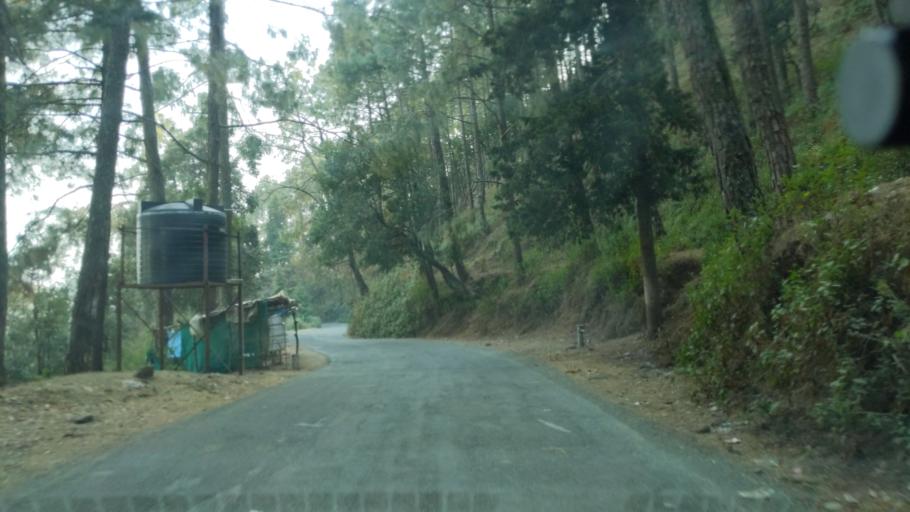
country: IN
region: Uttarakhand
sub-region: Naini Tal
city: Bhowali
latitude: 29.3965
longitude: 79.5381
